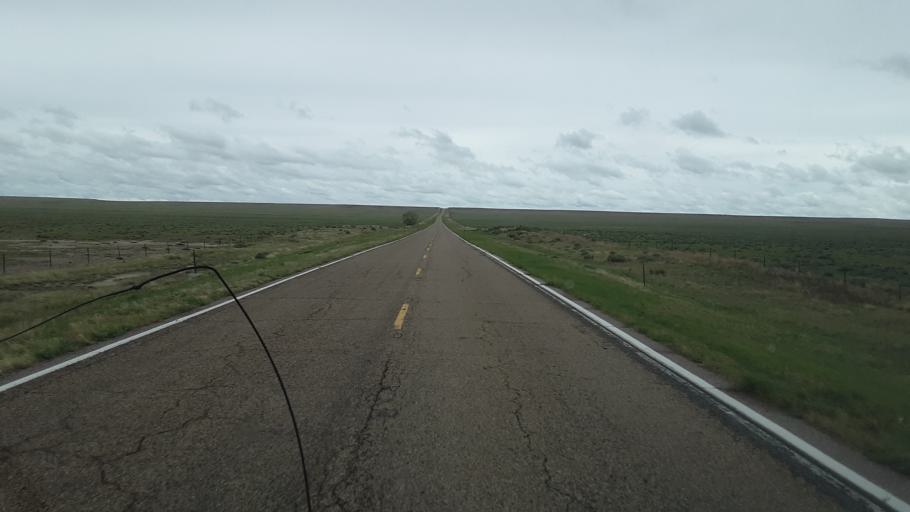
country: US
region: Colorado
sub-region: Lincoln County
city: Hugo
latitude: 38.8498
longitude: -103.3670
